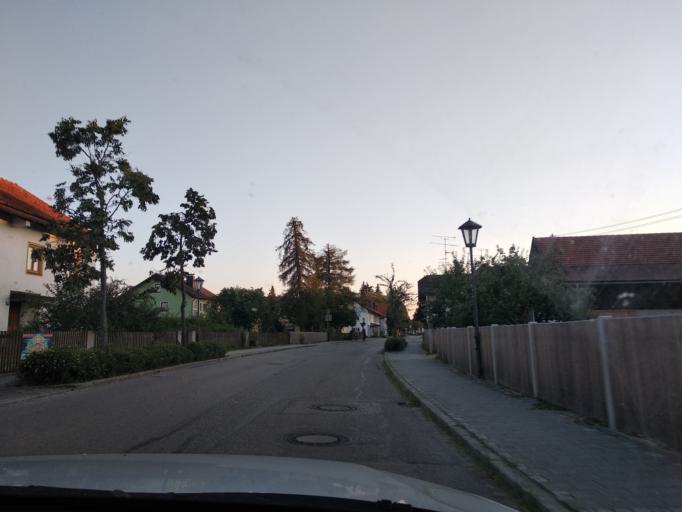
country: DE
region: Bavaria
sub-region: Upper Bavaria
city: Forstinning
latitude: 48.1644
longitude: 11.9089
